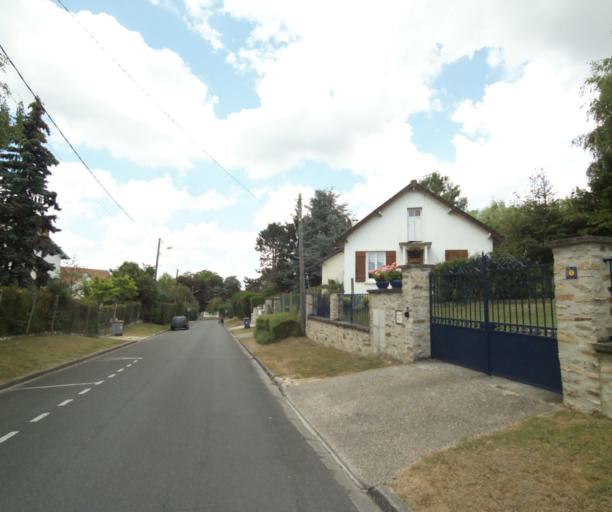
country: FR
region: Ile-de-France
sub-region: Departement de Seine-et-Marne
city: Hericy
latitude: 48.4491
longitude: 2.7688
